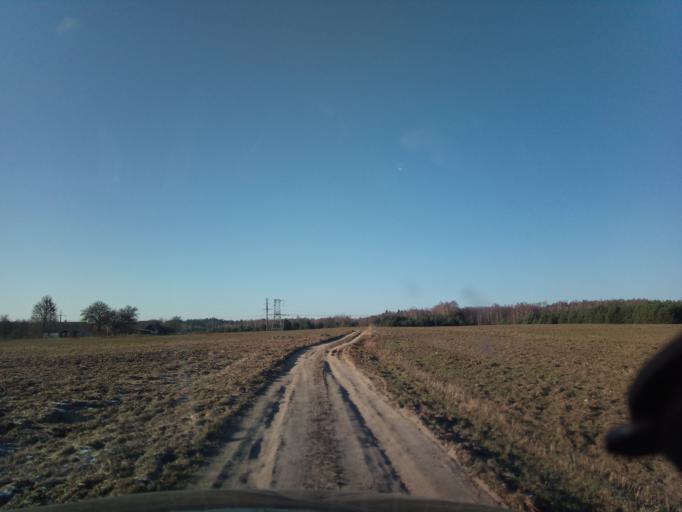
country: LT
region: Alytaus apskritis
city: Druskininkai
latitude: 53.9834
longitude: 23.9019
